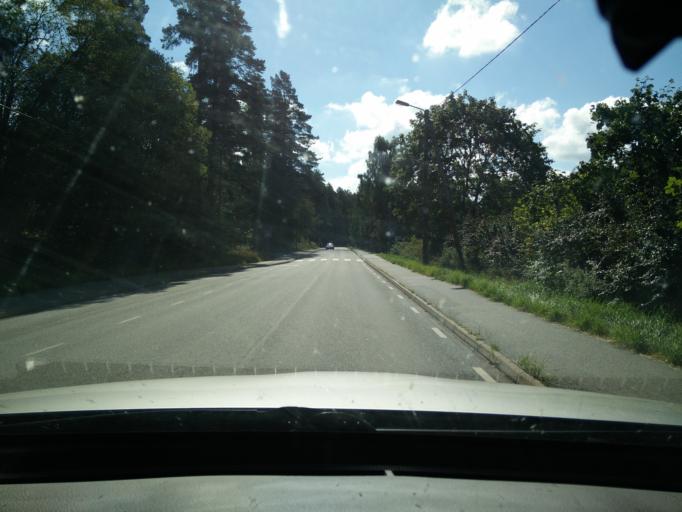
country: SE
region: Stockholm
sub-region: Lidingo
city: Lidingoe
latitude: 59.4592
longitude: 18.1870
